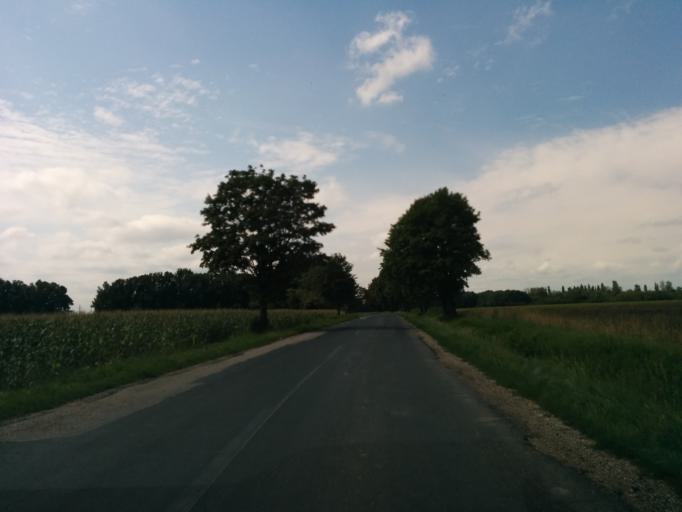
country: HU
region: Vas
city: Csepreg
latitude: 47.4754
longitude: 16.7335
